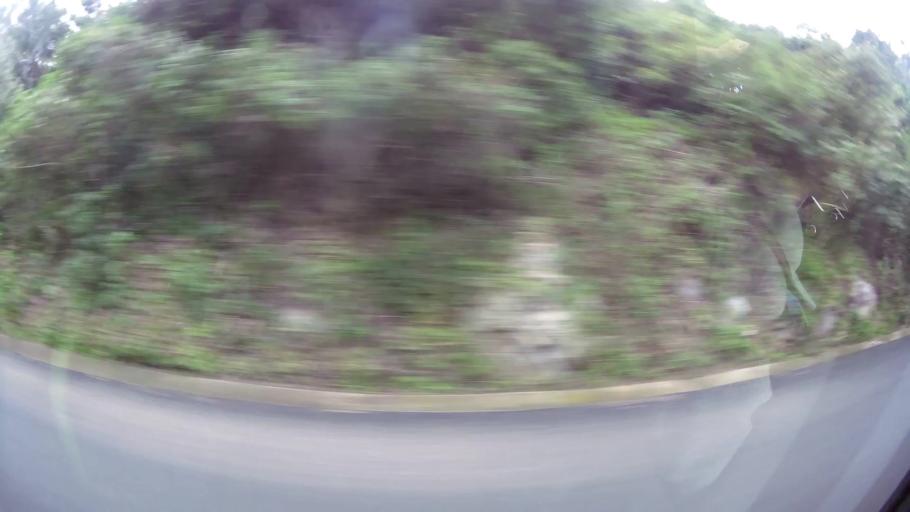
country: ZA
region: Western Cape
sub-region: Eden District Municipality
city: Plettenberg Bay
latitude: -34.0606
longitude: 23.3748
